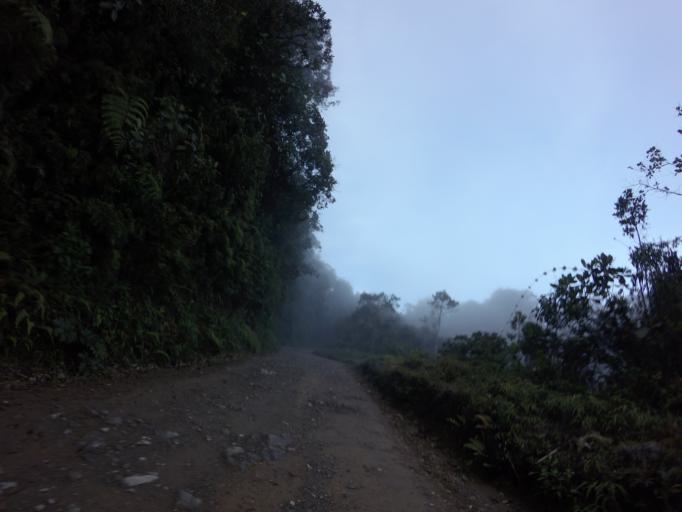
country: CO
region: Caldas
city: Pensilvania
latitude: 5.4109
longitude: -75.1315
